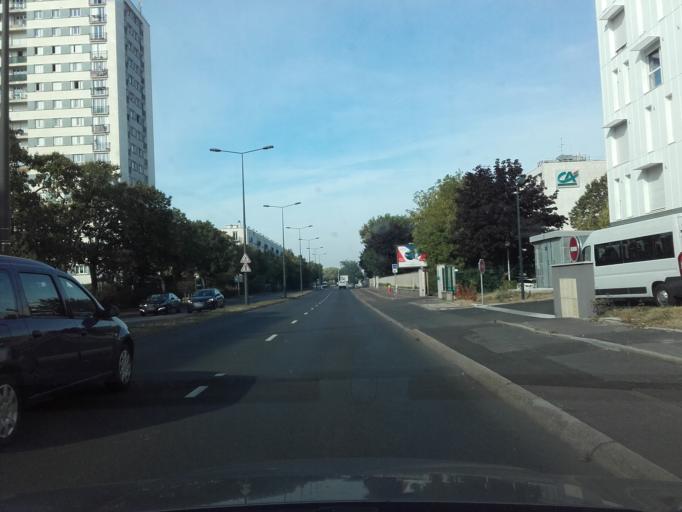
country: FR
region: Centre
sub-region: Departement d'Indre-et-Loire
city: Tours
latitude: 47.3737
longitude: 0.6833
